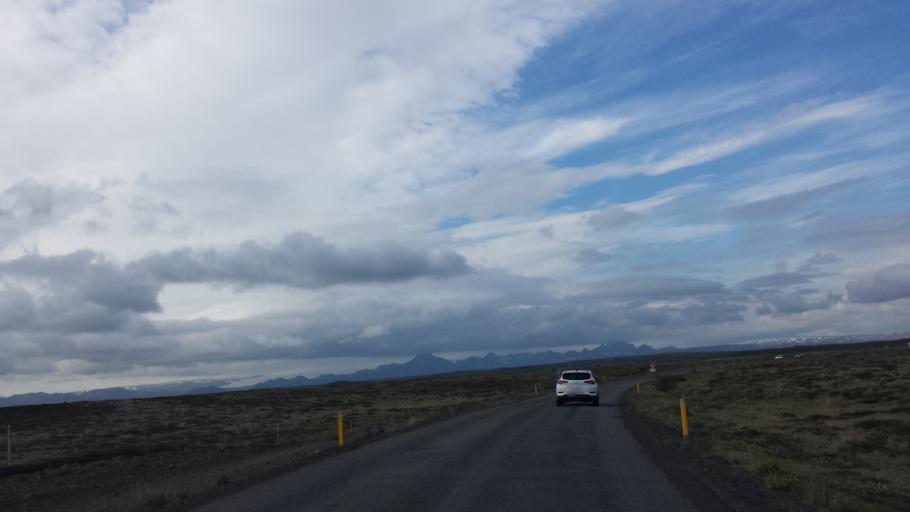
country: IS
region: South
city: Vestmannaeyjar
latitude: 64.3220
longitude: -20.1346
